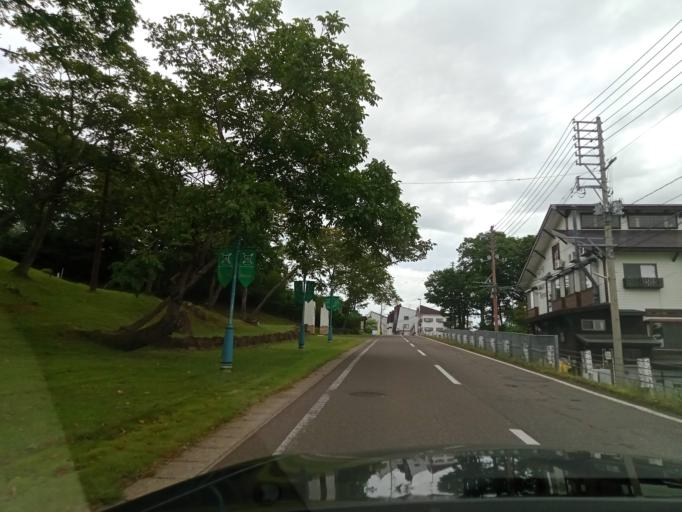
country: JP
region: Niigata
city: Arai
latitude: 36.8844
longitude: 138.1793
